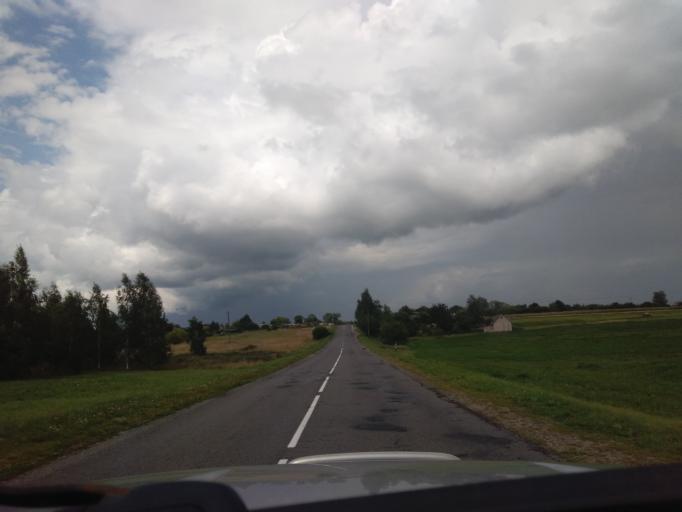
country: BY
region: Minsk
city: Tsimkavichy
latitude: 53.0602
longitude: 26.9872
